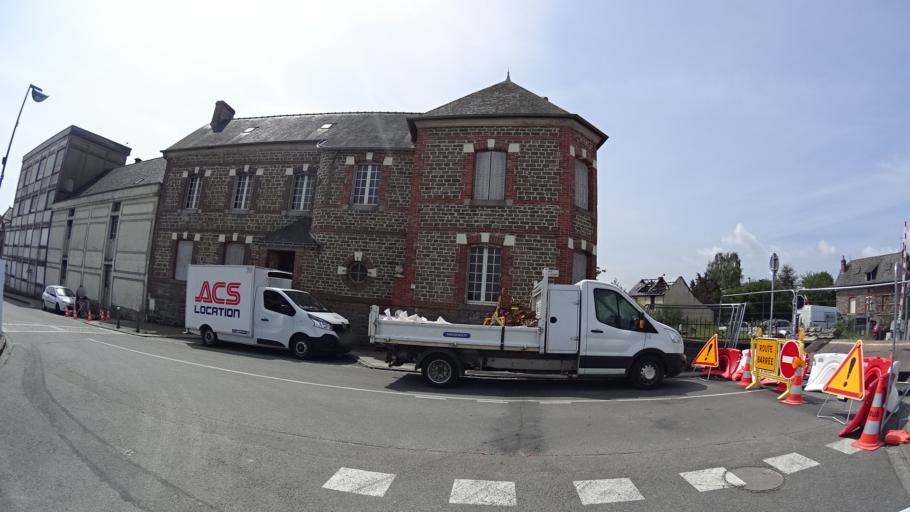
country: FR
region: Brittany
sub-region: Departement d'Ille-et-Vilaine
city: Saint-Armel
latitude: 48.0142
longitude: -1.5946
